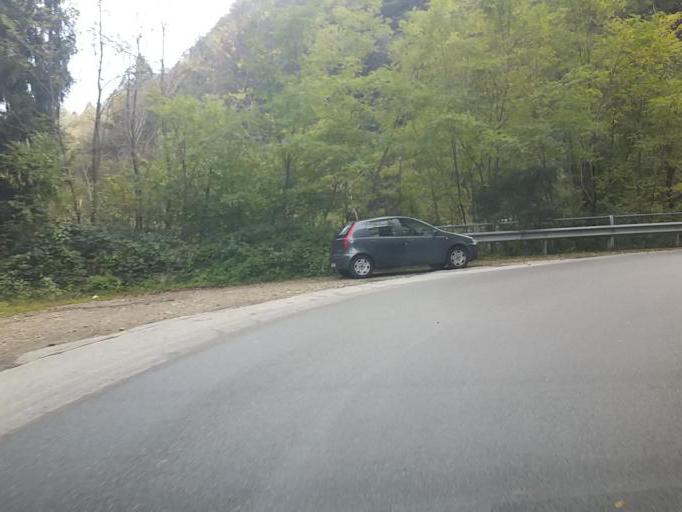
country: IT
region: Piedmont
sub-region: Provincia Verbano-Cusio-Ossola
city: Cavaglio-Spoccia
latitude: 46.0646
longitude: 8.6549
